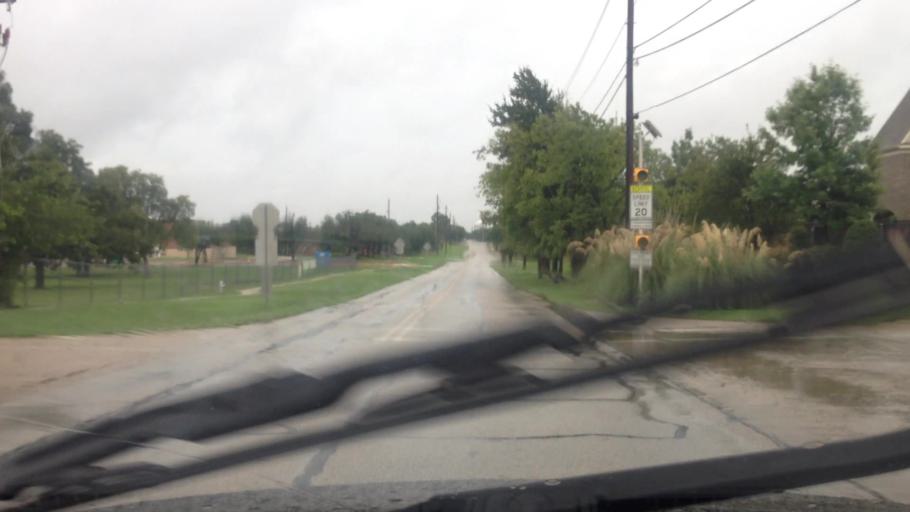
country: US
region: Texas
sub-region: Tarrant County
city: Keller
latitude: 32.9076
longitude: -97.2194
